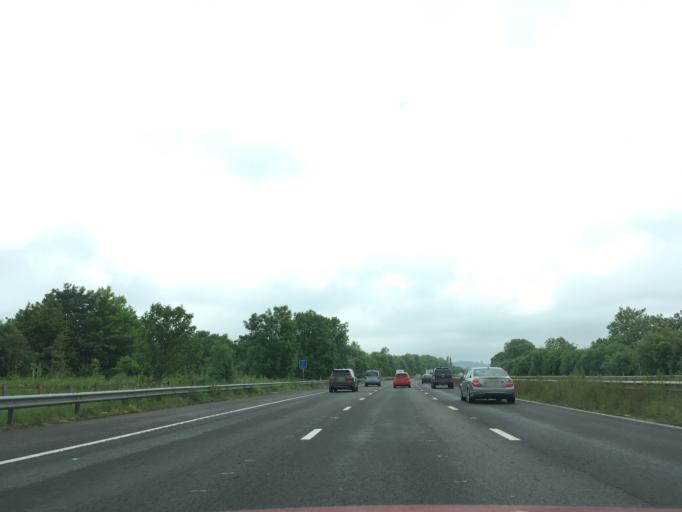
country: GB
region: England
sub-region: Devon
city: Bradninch
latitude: 50.8187
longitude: -3.4106
